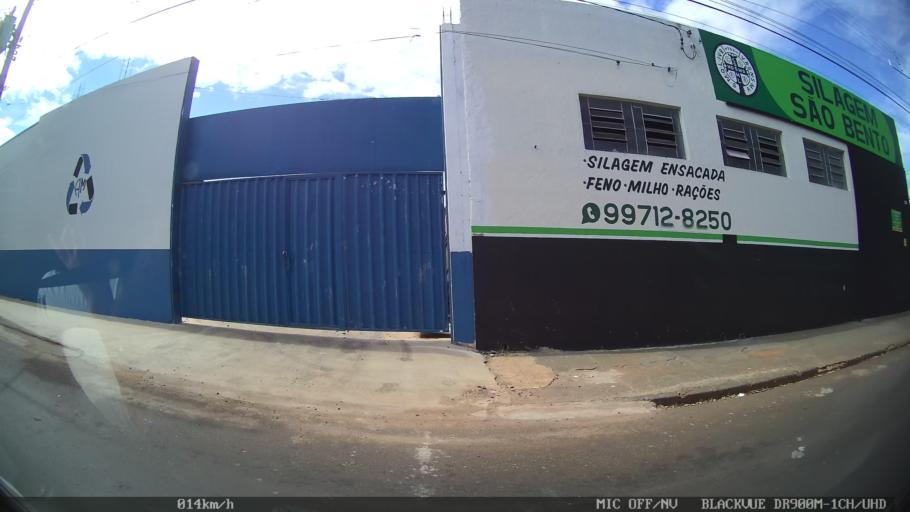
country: BR
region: Sao Paulo
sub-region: Bady Bassitt
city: Bady Bassitt
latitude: -20.8240
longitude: -49.5235
